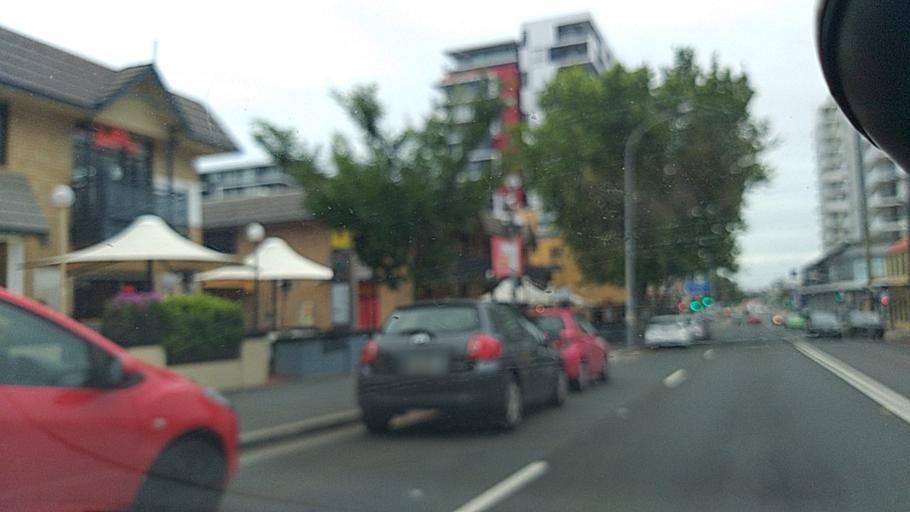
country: AU
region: New South Wales
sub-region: Wollongong
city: Wollongong
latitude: -34.4250
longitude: 150.9000
